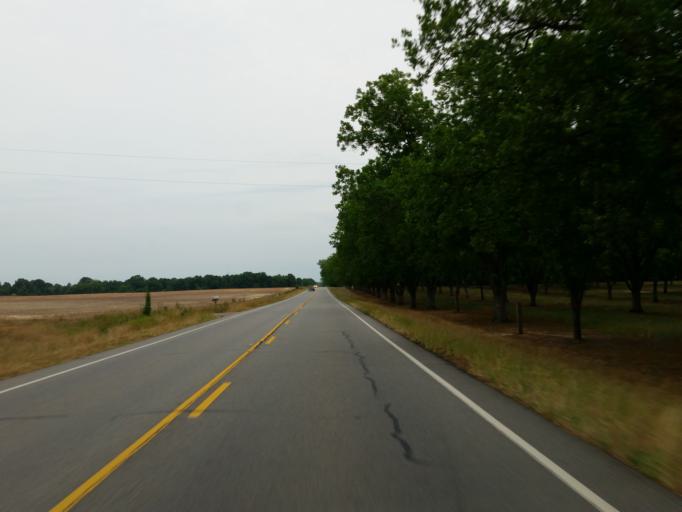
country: US
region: Georgia
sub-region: Dooly County
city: Unadilla
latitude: 32.2173
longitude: -83.7593
